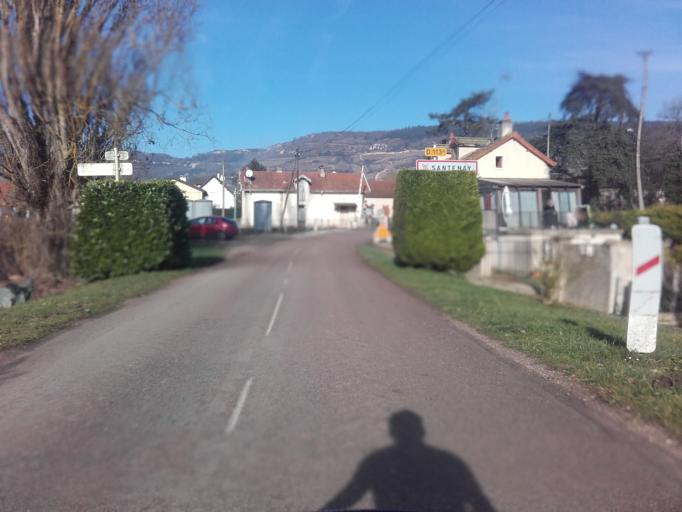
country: FR
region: Bourgogne
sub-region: Departement de Saone-et-Loire
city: Chagny
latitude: 46.9070
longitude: 4.6951
